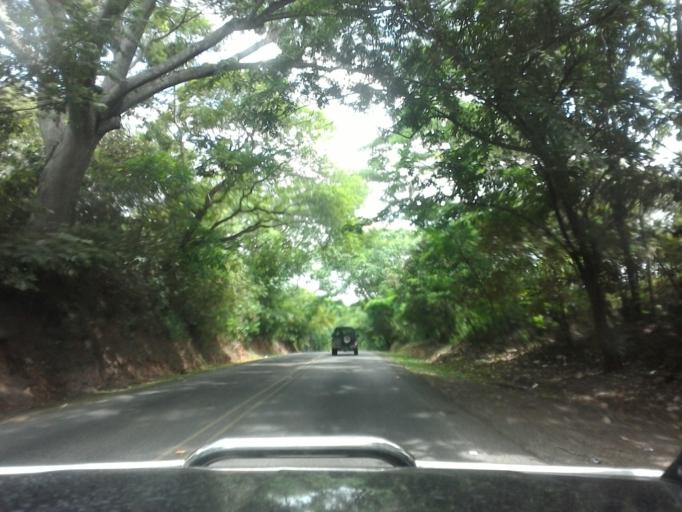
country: CR
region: Puntarenas
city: Miramar
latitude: 10.0791
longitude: -84.7818
